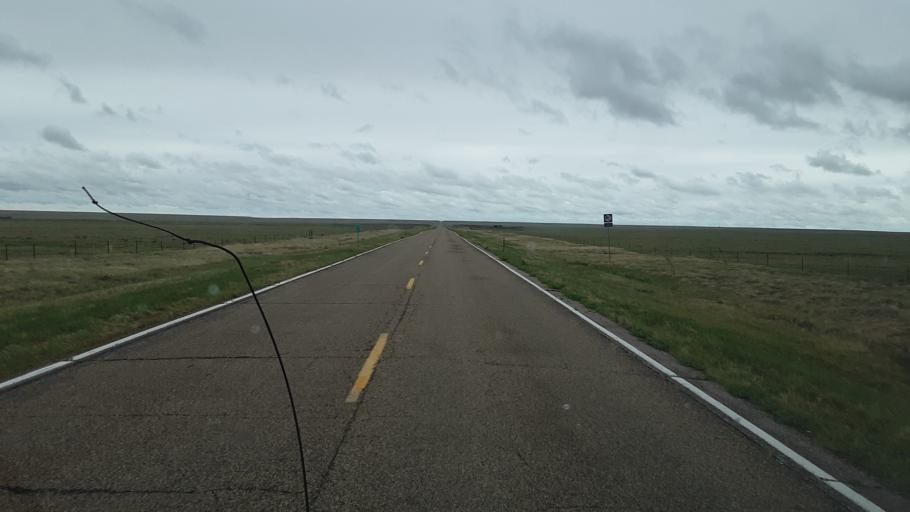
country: US
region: Colorado
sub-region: Lincoln County
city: Hugo
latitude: 38.8498
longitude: -103.3406
